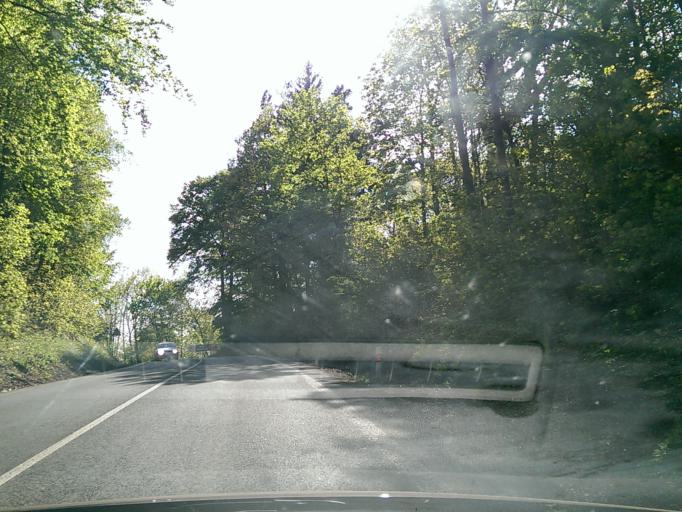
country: CZ
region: Liberecky
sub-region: Okres Semily
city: Turnov
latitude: 50.6168
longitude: 15.1668
